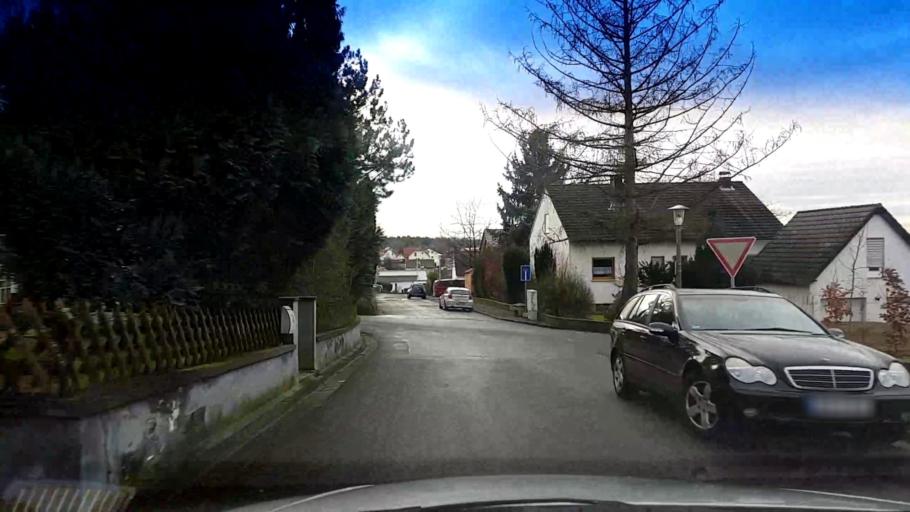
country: DE
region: Bavaria
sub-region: Upper Franconia
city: Litzendorf
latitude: 49.9082
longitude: 10.9929
